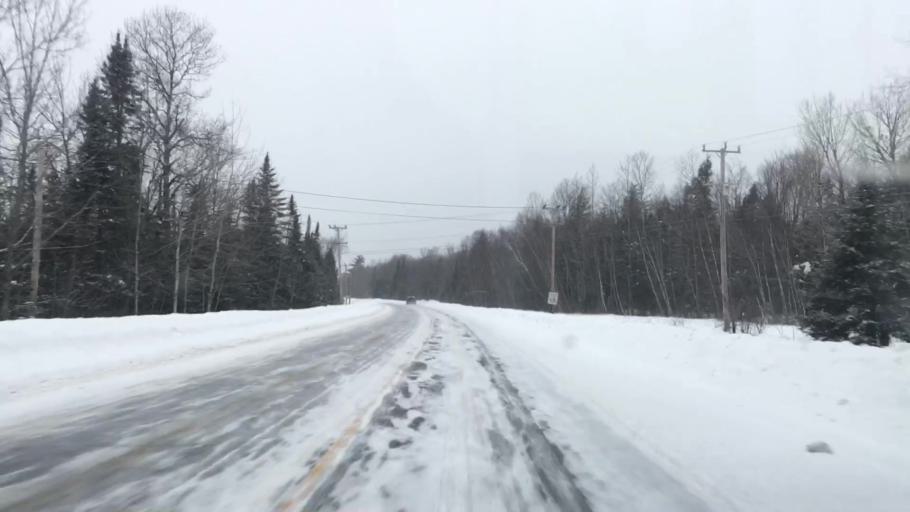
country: US
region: Maine
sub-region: Penobscot County
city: Medway
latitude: 45.5837
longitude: -68.4269
